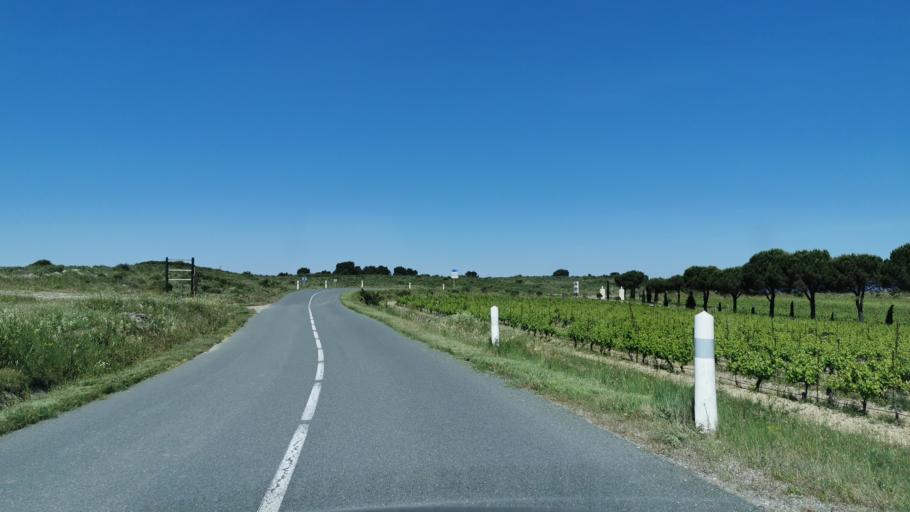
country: FR
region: Languedoc-Roussillon
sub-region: Departement de l'Aude
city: Armissan
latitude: 43.1748
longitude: 3.1104
